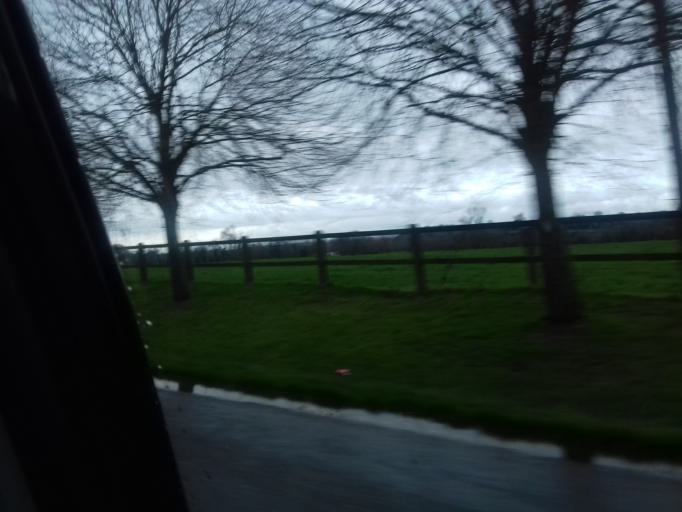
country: IE
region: Leinster
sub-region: County Carlow
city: Bagenalstown
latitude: 52.6337
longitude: -6.9941
